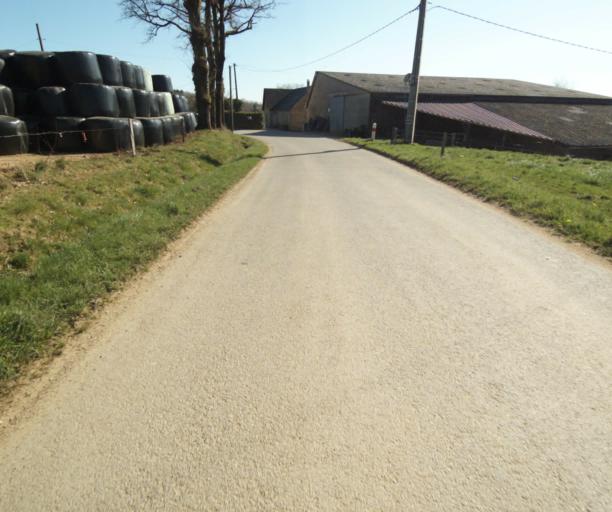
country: FR
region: Limousin
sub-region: Departement de la Correze
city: Chamboulive
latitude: 45.4740
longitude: 1.7188
